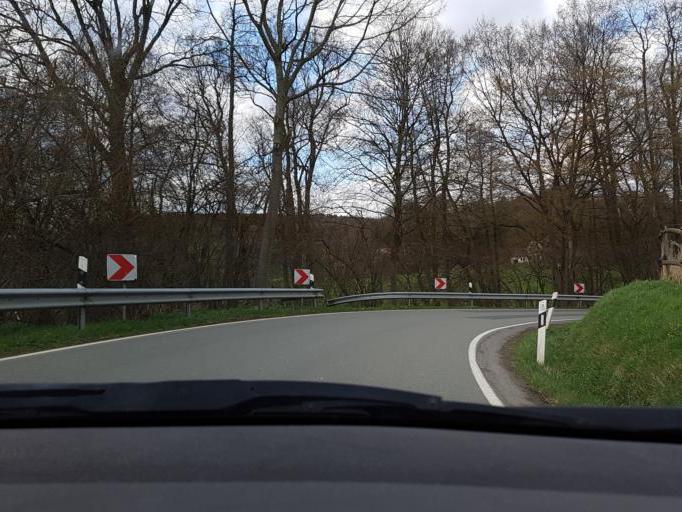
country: DE
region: Lower Saxony
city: Bodenfelde
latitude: 51.6835
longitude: 9.5263
